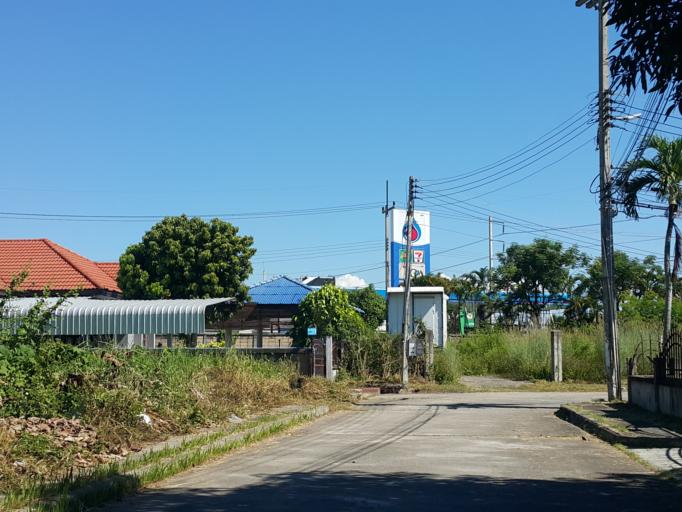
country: TH
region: Chiang Mai
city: San Sai
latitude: 18.8337
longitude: 99.0561
